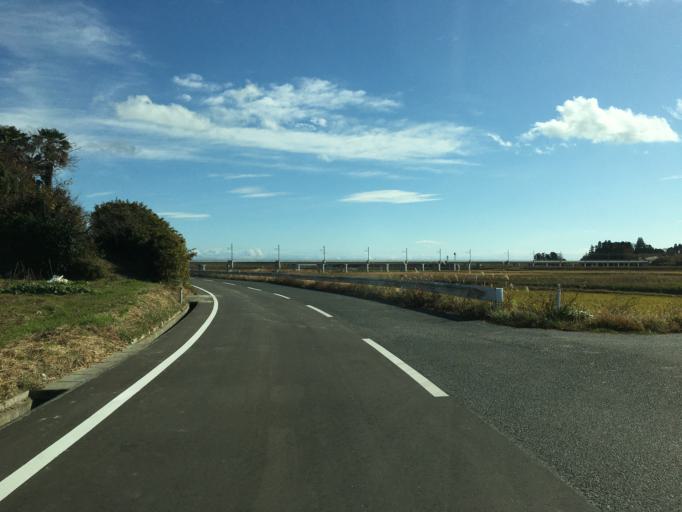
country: JP
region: Miyagi
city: Marumori
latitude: 37.8925
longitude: 140.9176
